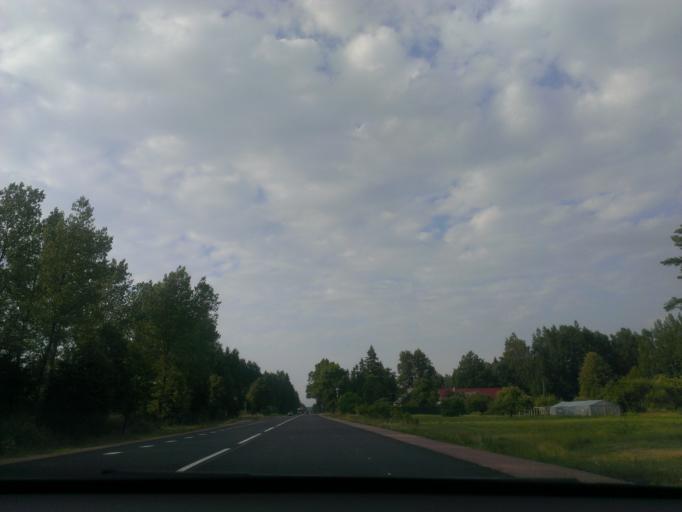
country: LV
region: Lecava
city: Iecava
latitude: 56.6920
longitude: 24.2414
